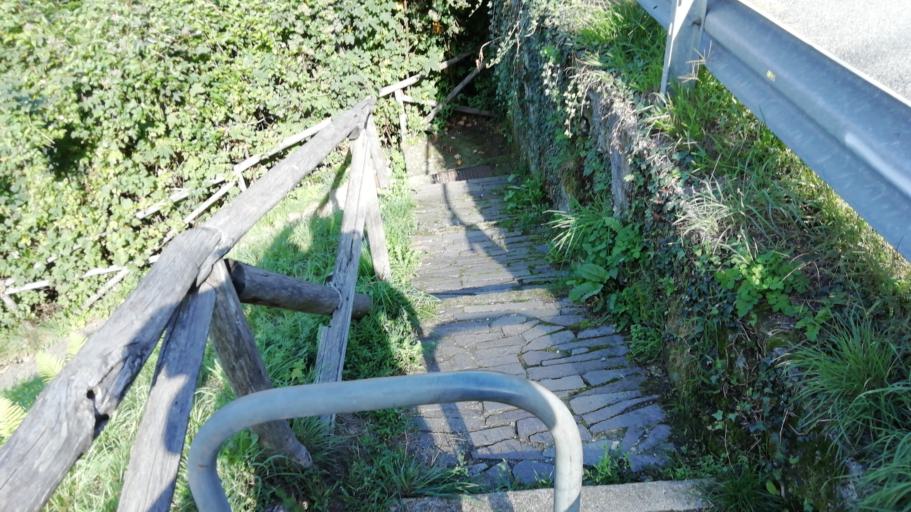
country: IT
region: Liguria
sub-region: Provincia di Genova
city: Masone
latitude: 44.4998
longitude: 8.7162
